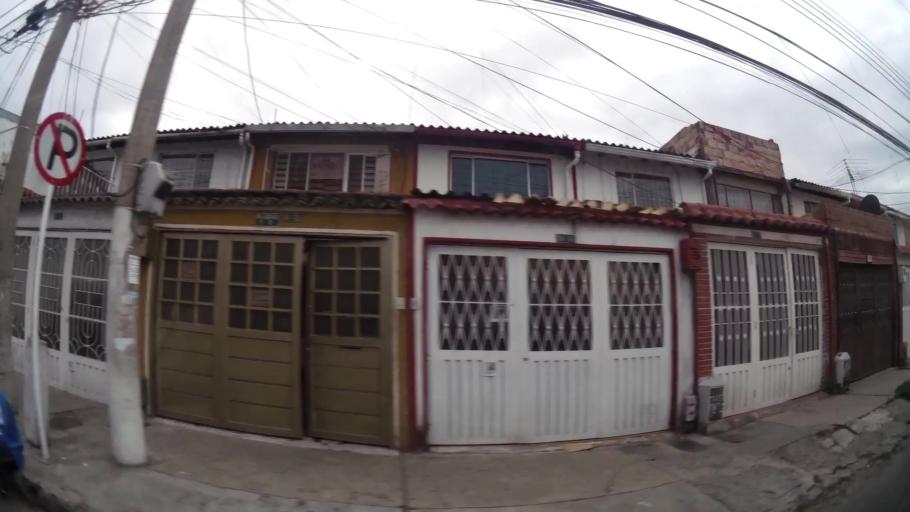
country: CO
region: Bogota D.C.
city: Bogota
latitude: 4.6896
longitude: -74.1079
